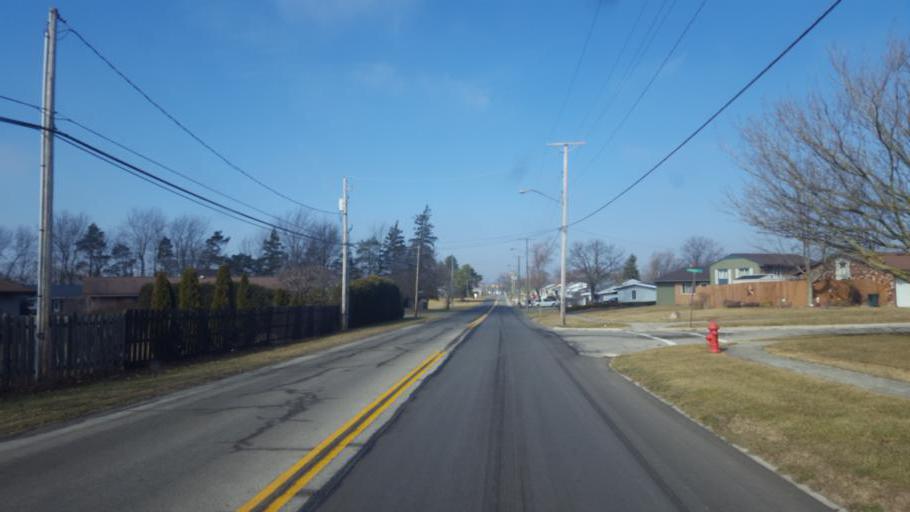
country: US
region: Ohio
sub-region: Crawford County
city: Bucyrus
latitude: 40.7949
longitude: -82.9557
